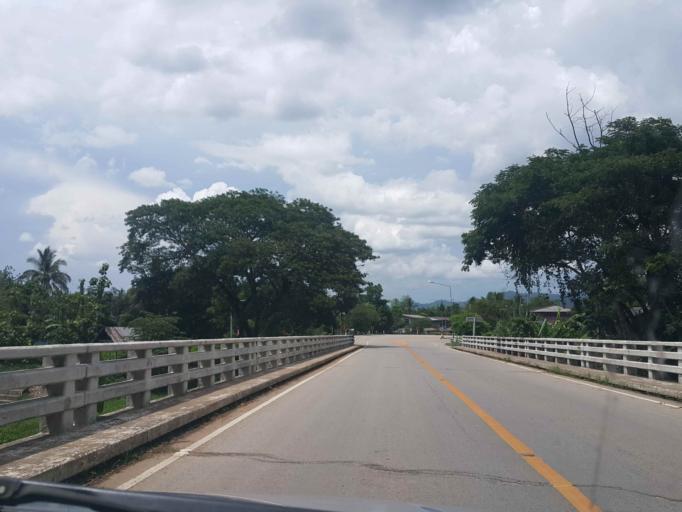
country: TH
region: Nan
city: Ban Luang
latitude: 18.8477
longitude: 100.4227
